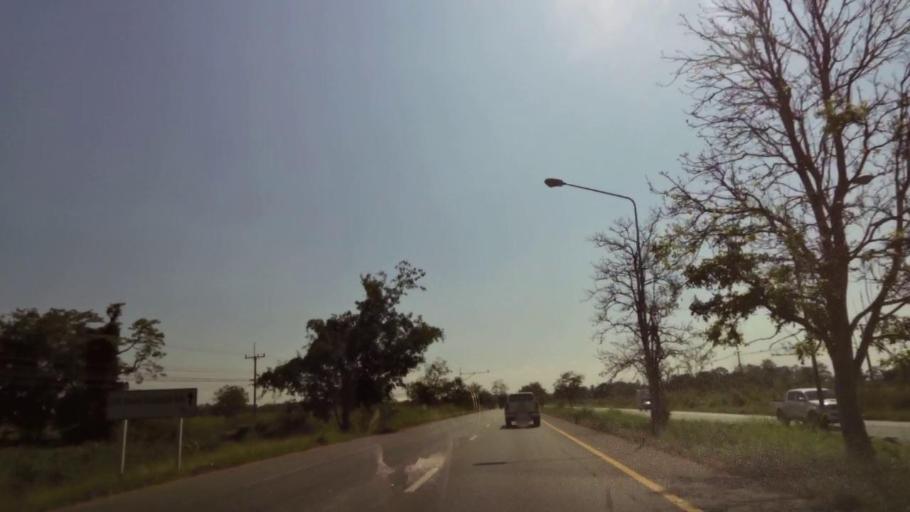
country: TH
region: Nakhon Sawan
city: Kao Liao
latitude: 15.8613
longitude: 100.1168
